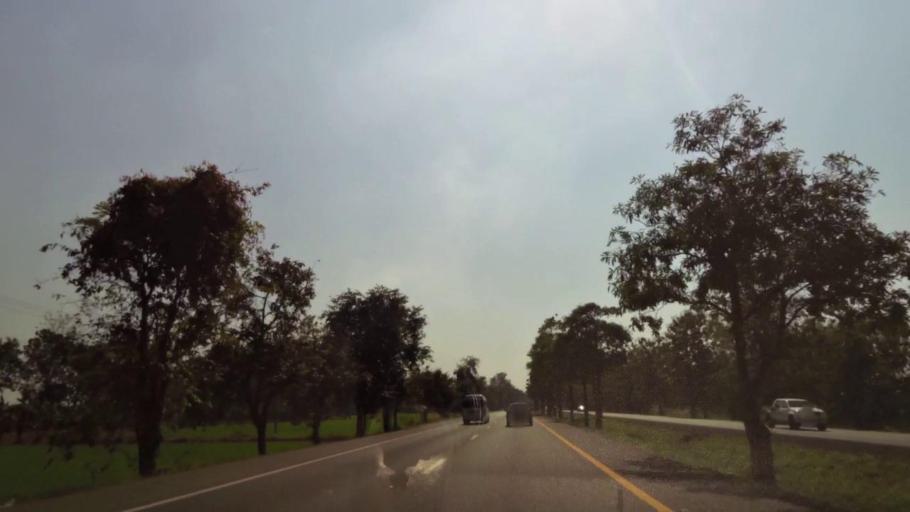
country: TH
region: Phichit
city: Bueng Na Rang
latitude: 16.0676
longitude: 100.1237
